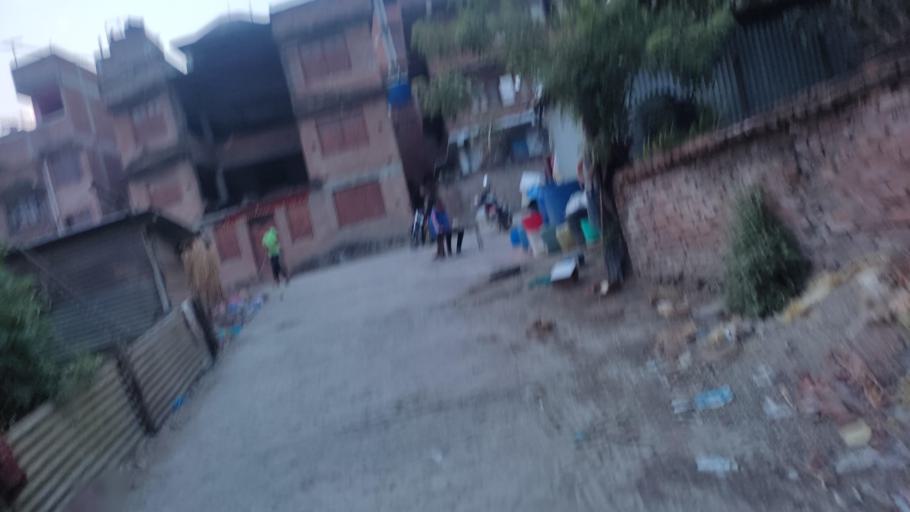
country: NP
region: Central Region
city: Kirtipur
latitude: 27.6688
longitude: 85.2777
